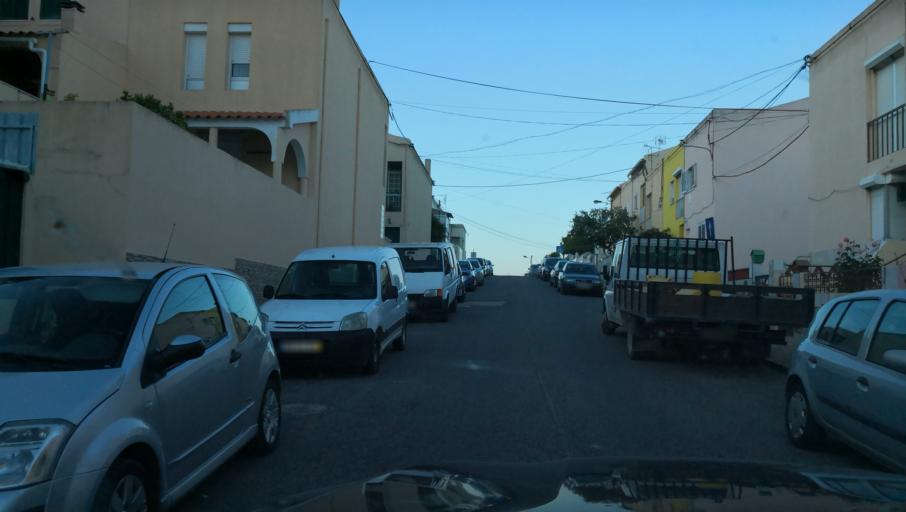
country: PT
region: Setubal
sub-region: Setubal
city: Setubal
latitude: 38.5251
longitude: -8.9131
